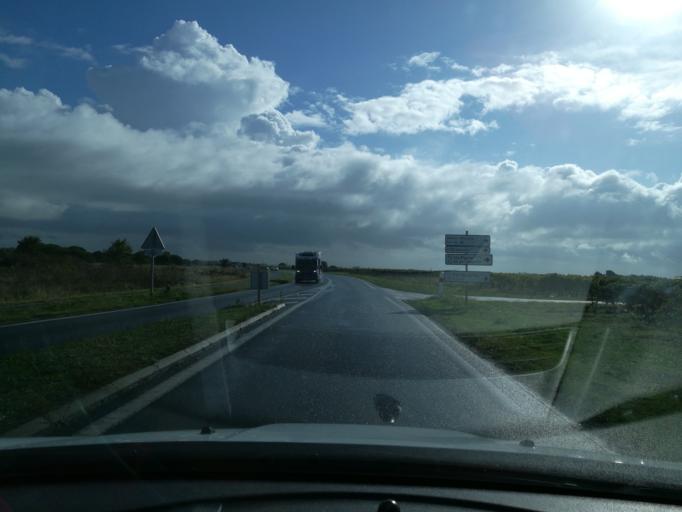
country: FR
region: Poitou-Charentes
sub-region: Departement de la Charente-Maritime
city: Sainte-Marie-de-Re
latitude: 46.1531
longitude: -1.3045
